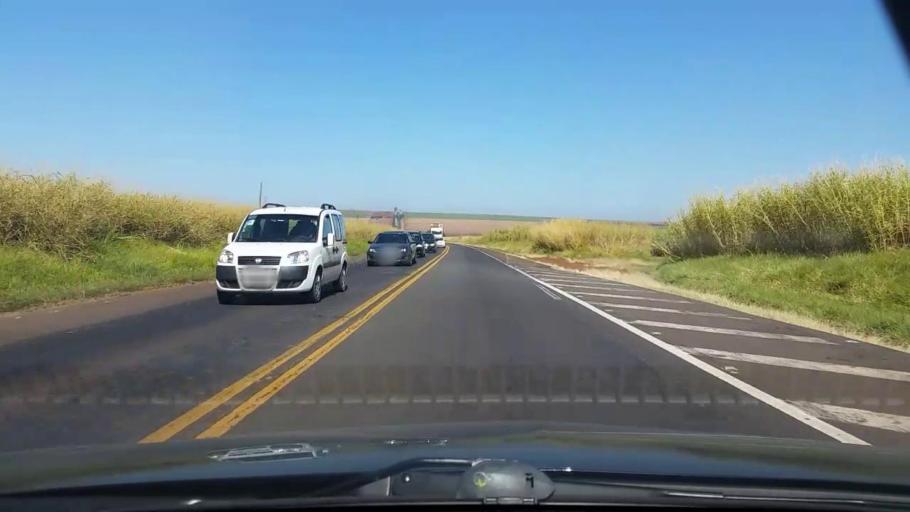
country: BR
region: Sao Paulo
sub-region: Jau
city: Jau
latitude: -22.3563
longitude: -48.5725
